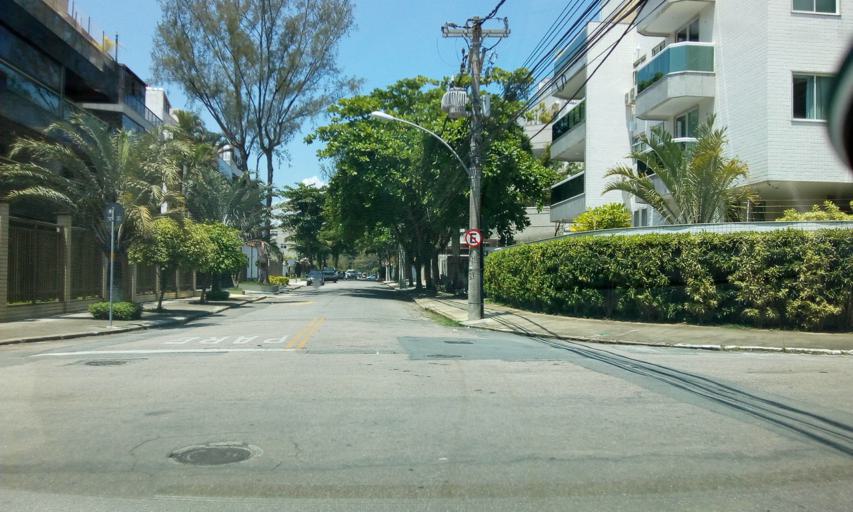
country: BR
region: Rio de Janeiro
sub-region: Nilopolis
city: Nilopolis
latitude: -23.0255
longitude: -43.4641
